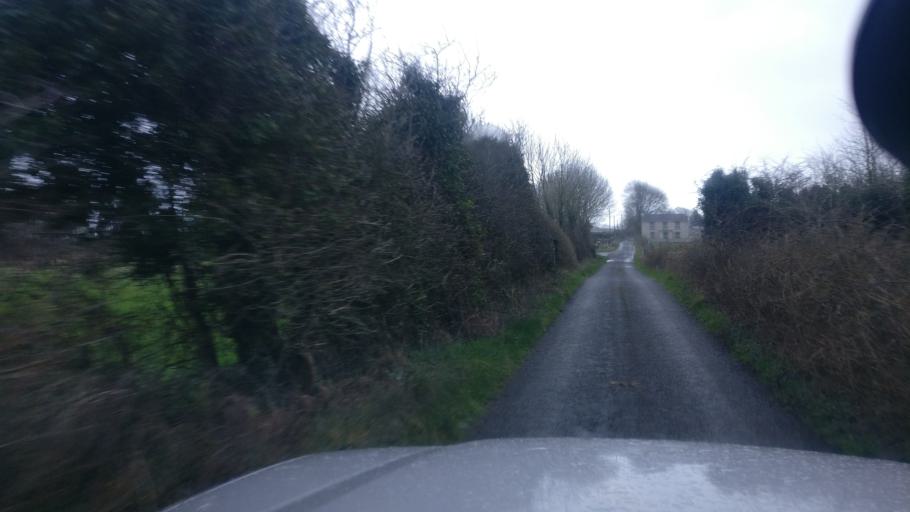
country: IE
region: Connaught
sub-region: County Galway
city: Loughrea
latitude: 53.2442
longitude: -8.4251
